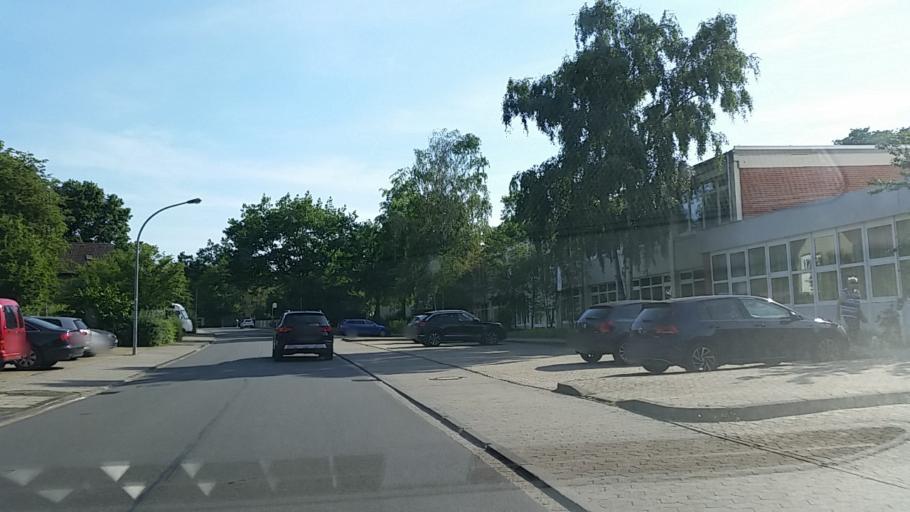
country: DE
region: Lower Saxony
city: Weyhausen
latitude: 52.4126
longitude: 10.7238
